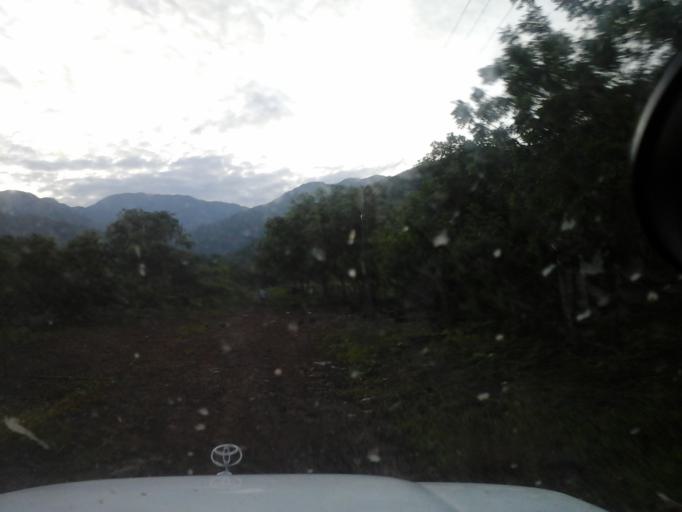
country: CO
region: Cesar
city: Agustin Codazzi
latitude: 10.1712
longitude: -73.1615
